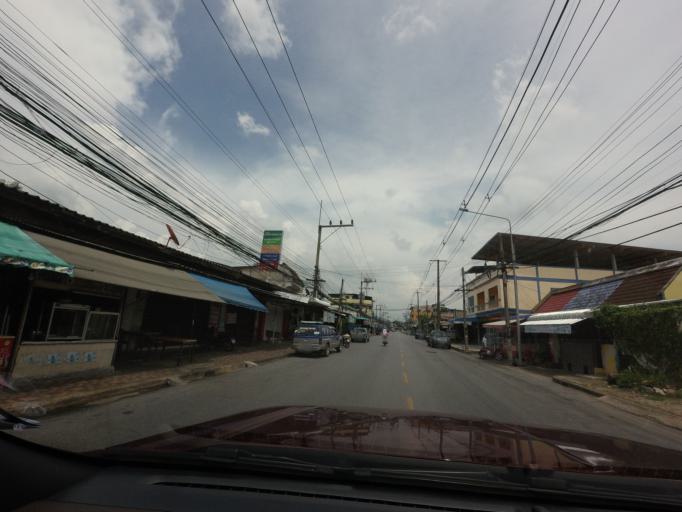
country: TH
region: Yala
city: Yala
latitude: 6.5361
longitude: 101.2868
